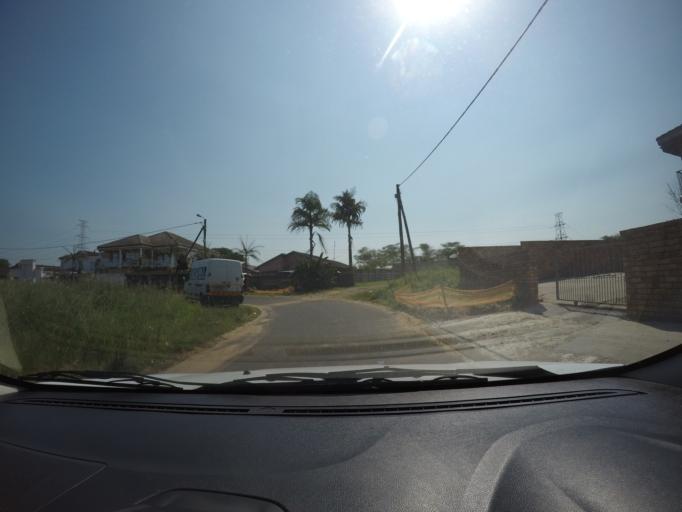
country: ZA
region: KwaZulu-Natal
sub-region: uThungulu District Municipality
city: Richards Bay
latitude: -28.7254
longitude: 32.0368
